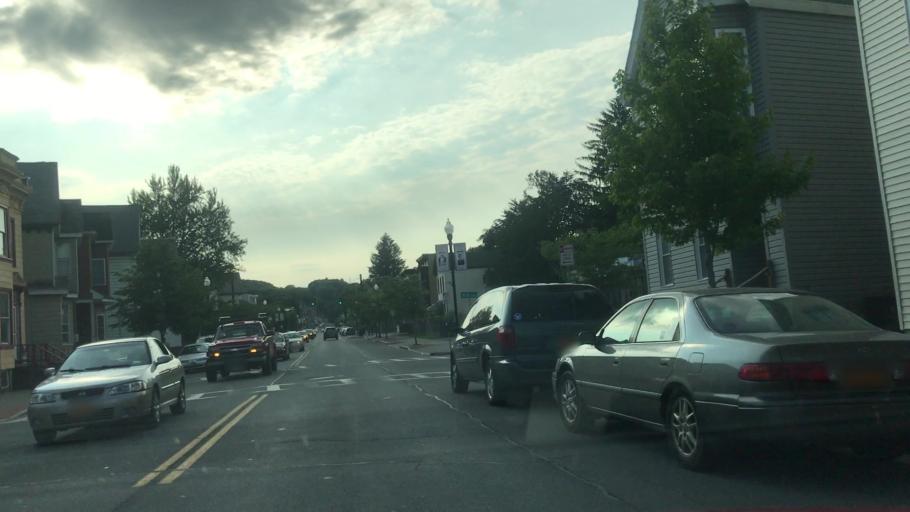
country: US
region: New York
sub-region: Albany County
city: Watervliet
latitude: 42.7318
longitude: -73.7074
